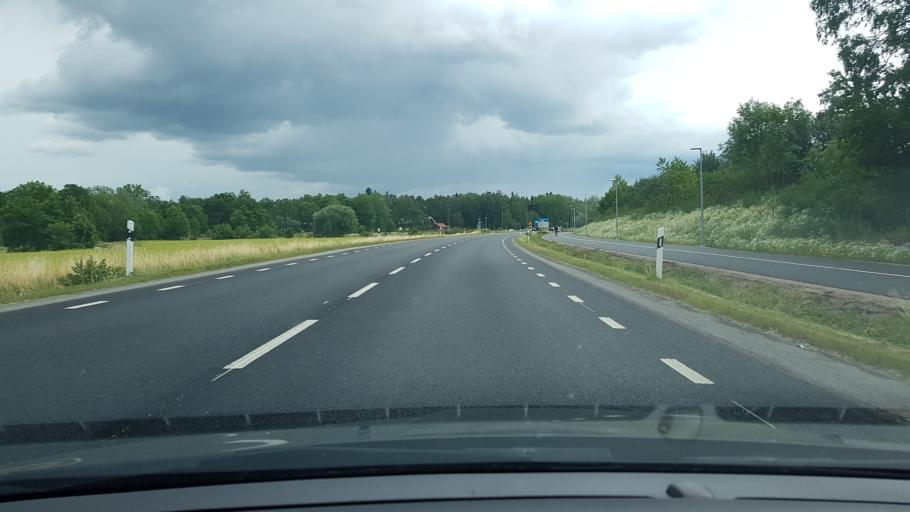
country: SE
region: Uppsala
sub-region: Uppsala Kommun
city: Saevja
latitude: 59.8234
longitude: 17.6985
